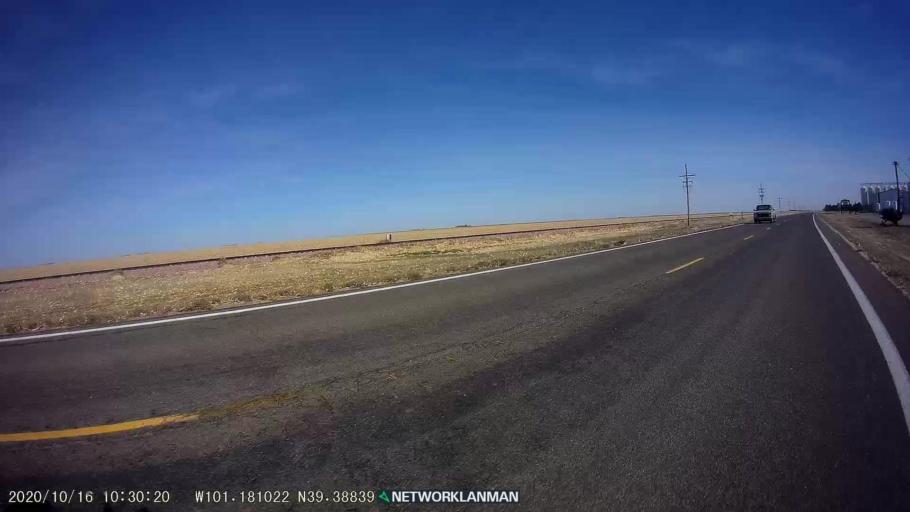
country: US
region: Kansas
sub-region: Thomas County
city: Colby
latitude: 39.3881
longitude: -101.1805
